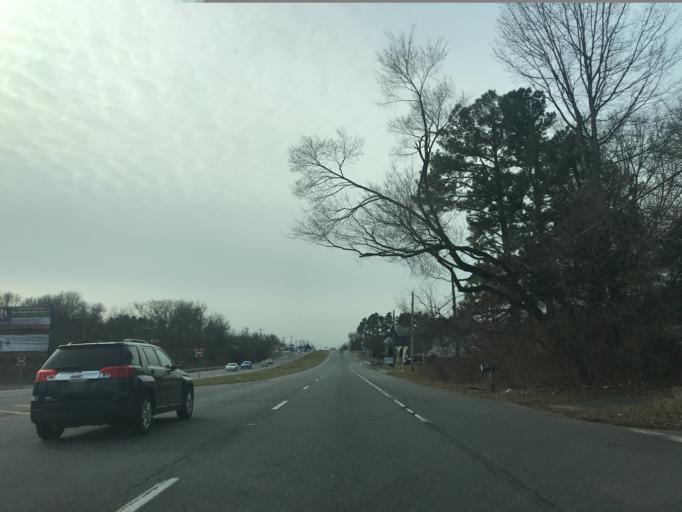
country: US
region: Delaware
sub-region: New Castle County
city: Bear
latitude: 39.6446
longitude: -75.6396
